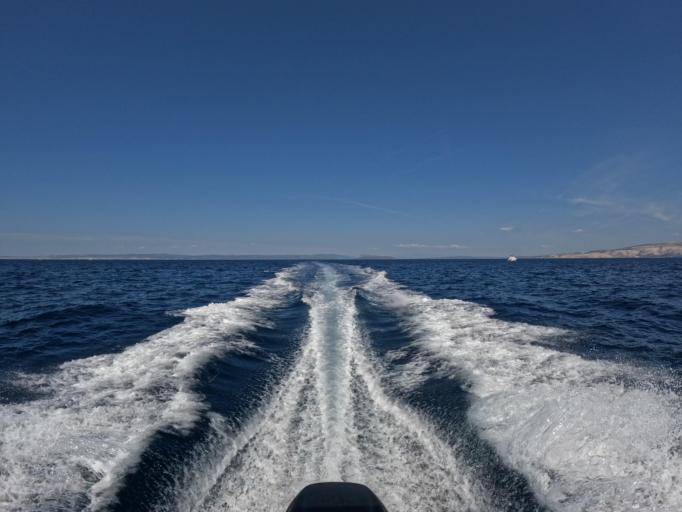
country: HR
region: Primorsko-Goranska
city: Lopar
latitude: 44.8722
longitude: 14.6685
